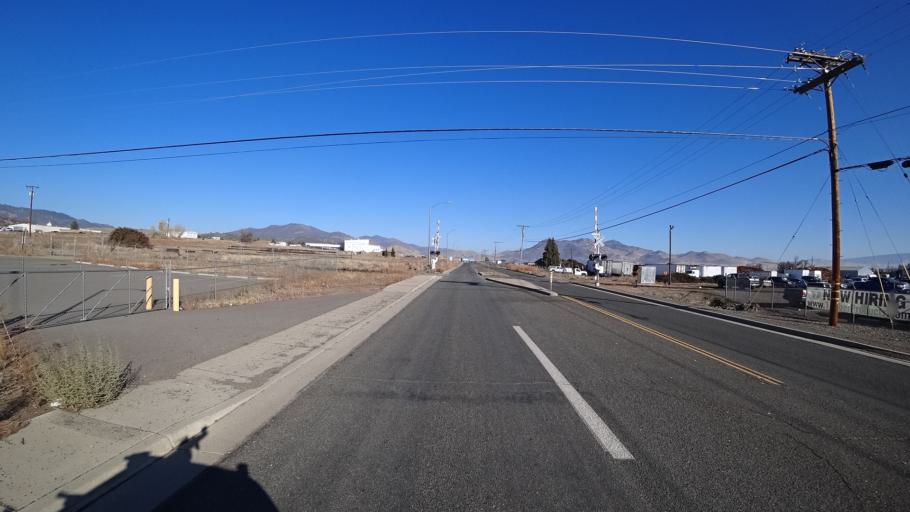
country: US
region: California
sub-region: Siskiyou County
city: Yreka
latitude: 41.7312
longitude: -122.5934
